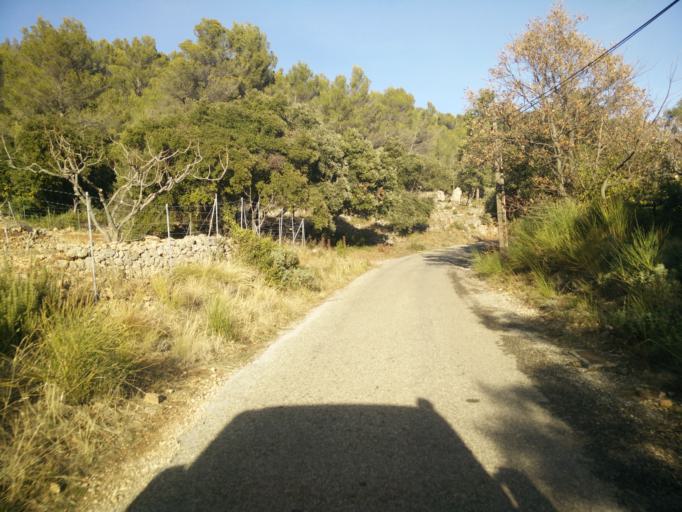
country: FR
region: Provence-Alpes-Cote d'Azur
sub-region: Departement du Var
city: Belgentier
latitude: 43.2089
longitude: 5.9793
